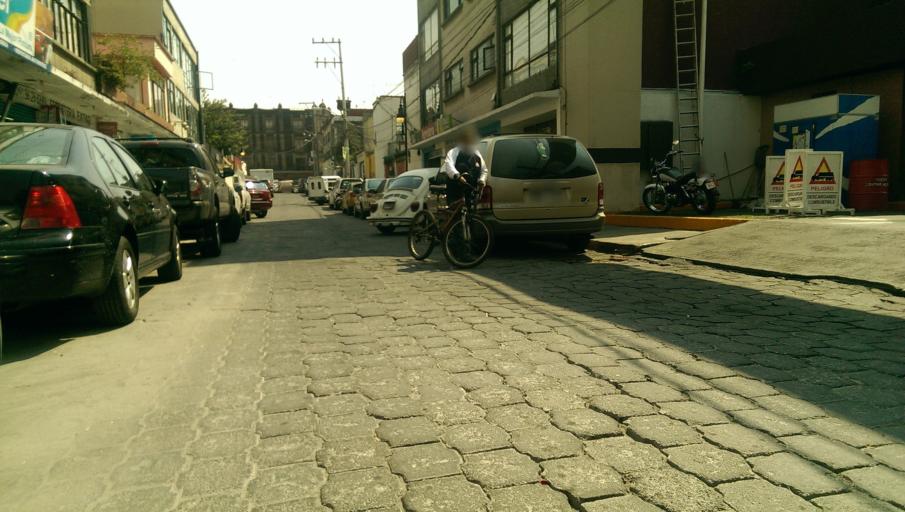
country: MX
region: Mexico City
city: Coyoacan
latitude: 19.3507
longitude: -99.1638
